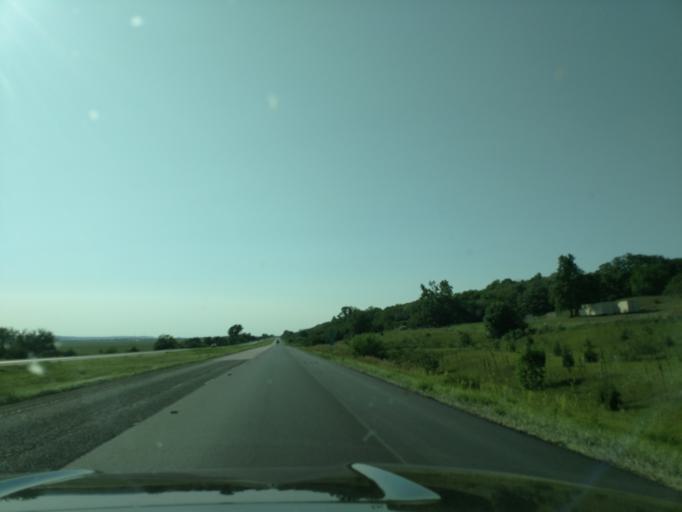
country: US
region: Missouri
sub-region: Holt County
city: Mound City
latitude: 40.2148
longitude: -95.3826
